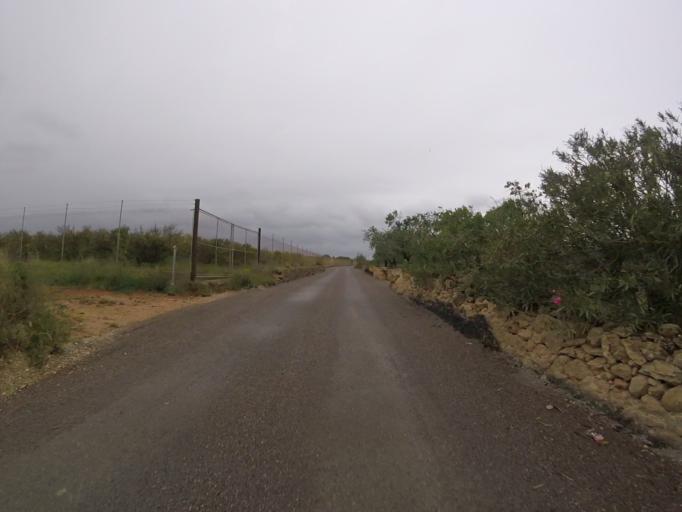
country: ES
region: Valencia
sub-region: Provincia de Castello
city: Alcoceber
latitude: 40.2371
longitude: 0.2528
